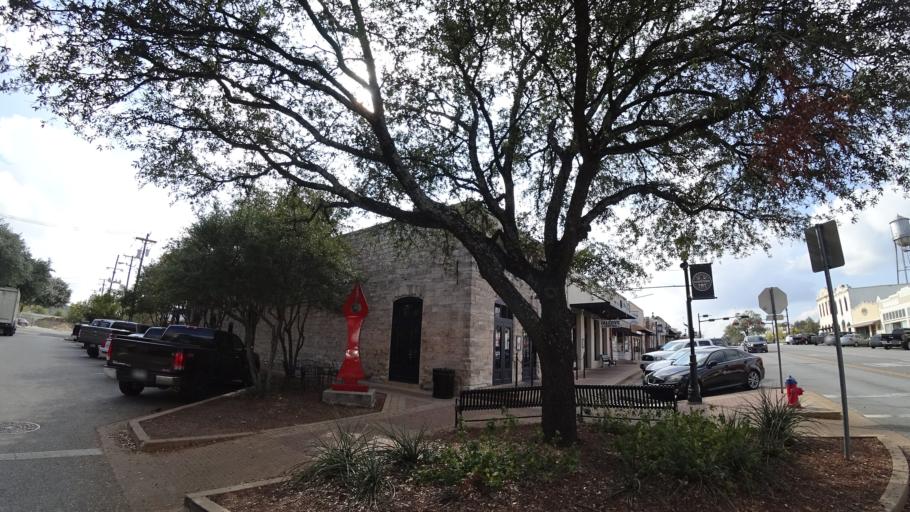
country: US
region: Texas
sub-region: Williamson County
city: Round Rock
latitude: 30.5088
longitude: -97.6778
